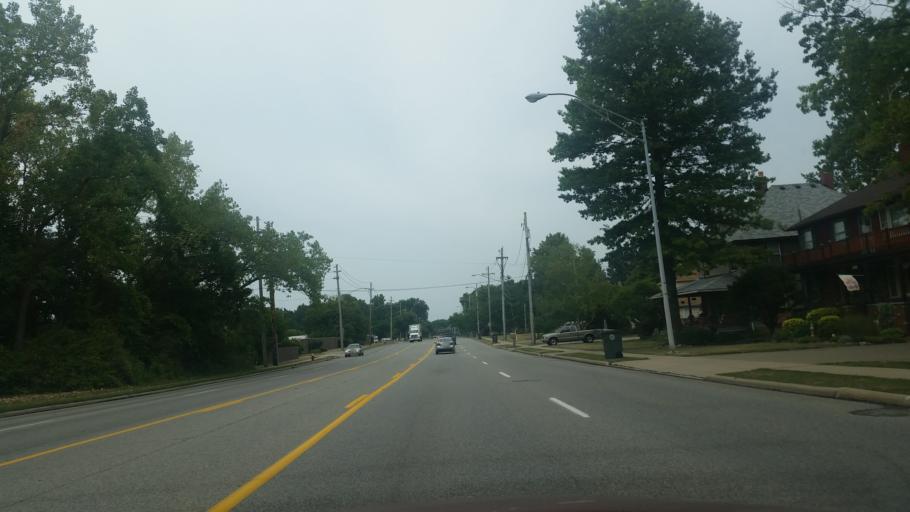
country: US
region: Ohio
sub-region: Cuyahoga County
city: Brooklyn
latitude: 41.4316
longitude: -81.7626
